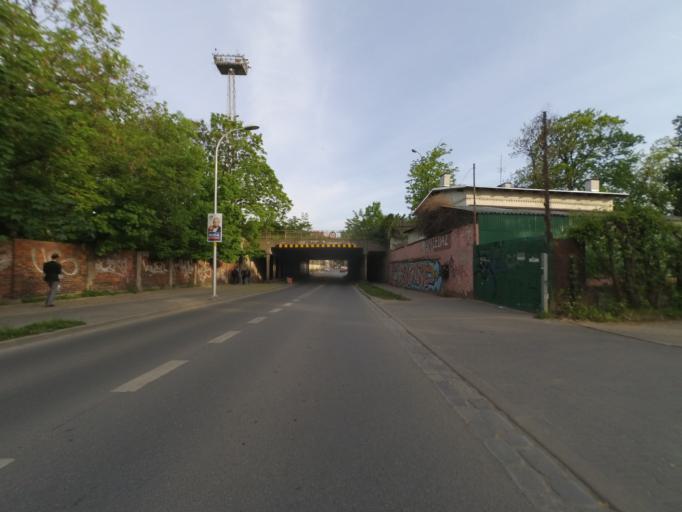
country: PL
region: Lower Silesian Voivodeship
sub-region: Powiat wroclawski
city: Wroclaw
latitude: 51.1285
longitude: 17.0470
